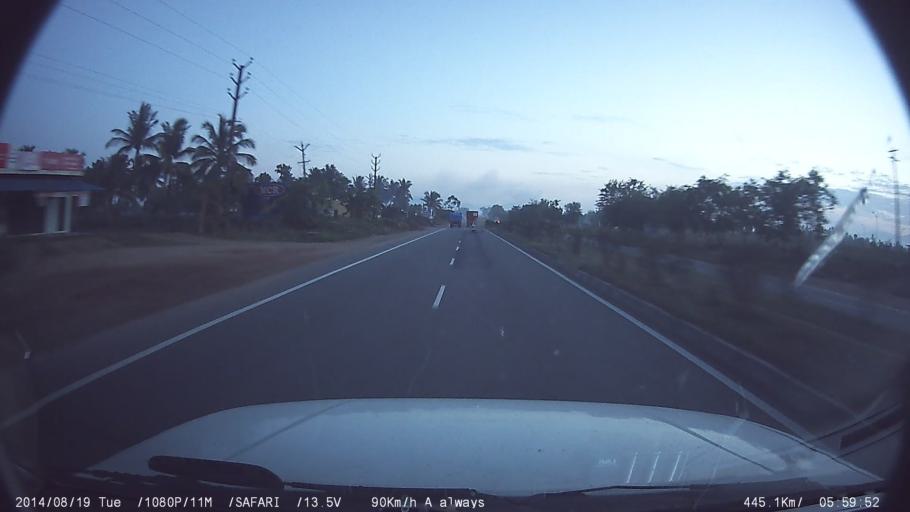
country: IN
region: Tamil Nadu
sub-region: Salem
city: Omalur
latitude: 11.8000
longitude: 78.0576
